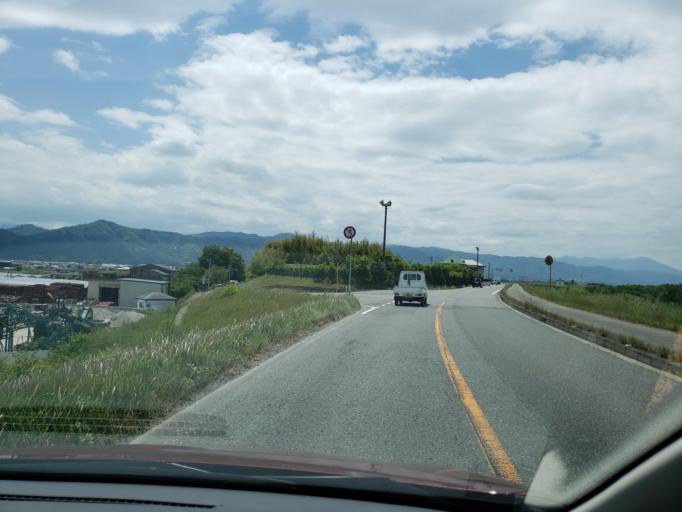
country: JP
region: Tokushima
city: Ishii
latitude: 34.0928
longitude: 134.4160
